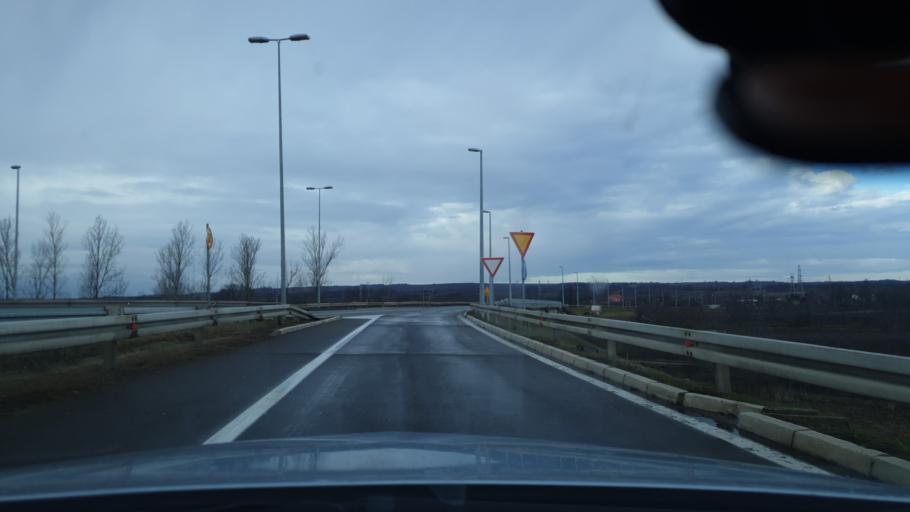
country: RS
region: Central Serbia
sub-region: Podunavski Okrug
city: Smederevo
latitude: 44.5854
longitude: 20.9609
